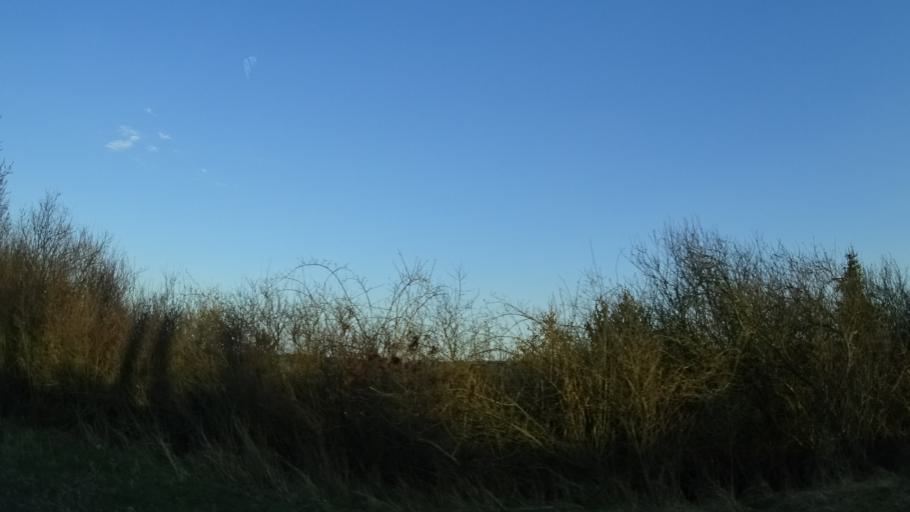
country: DE
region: Rheinland-Pfalz
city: Nieder-Wiesen
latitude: 49.7261
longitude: 7.9622
